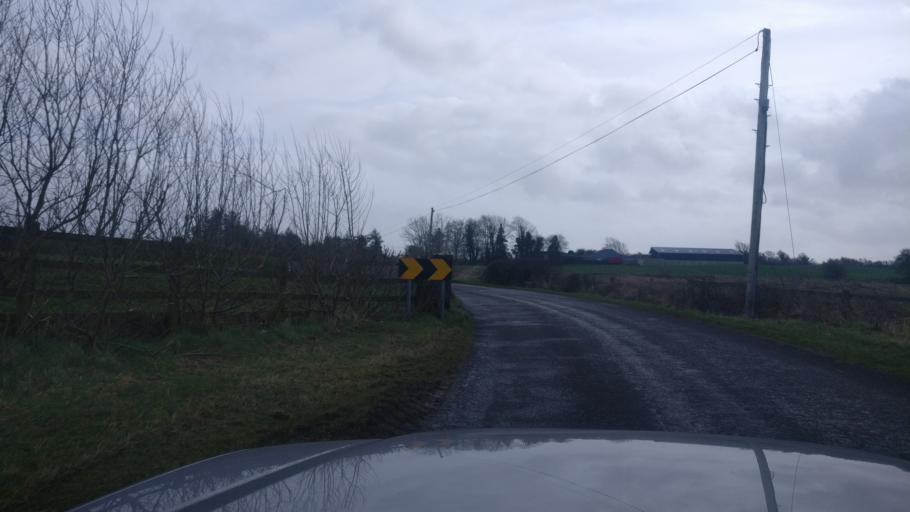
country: IE
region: Connaught
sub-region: County Galway
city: Loughrea
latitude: 53.2840
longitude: -8.4653
